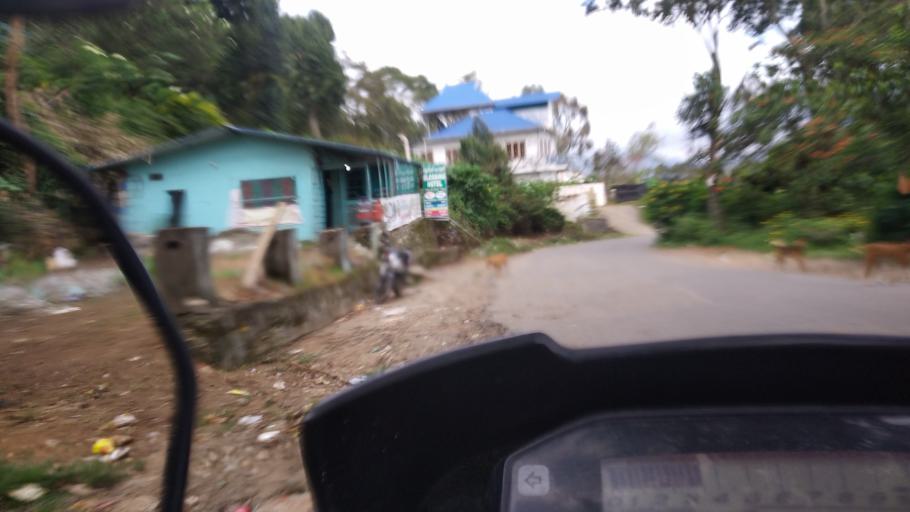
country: IN
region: Kerala
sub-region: Idukki
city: Munnar
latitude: 10.0412
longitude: 77.1758
